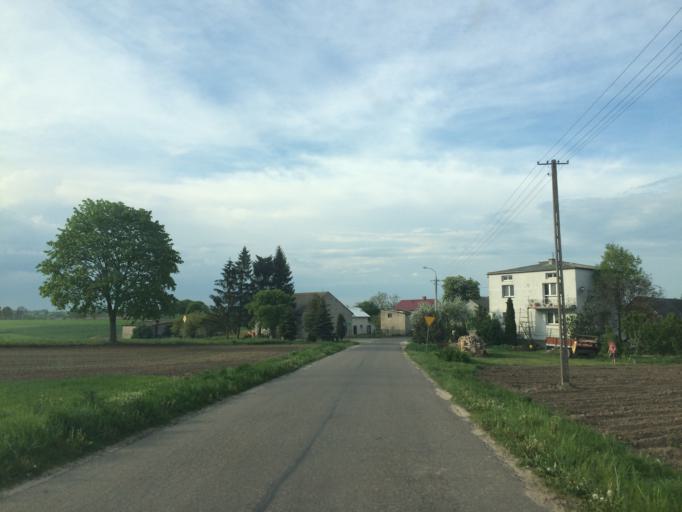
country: PL
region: Kujawsko-Pomorskie
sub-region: Powiat brodnicki
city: Brzozie
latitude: 53.3534
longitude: 19.6015
